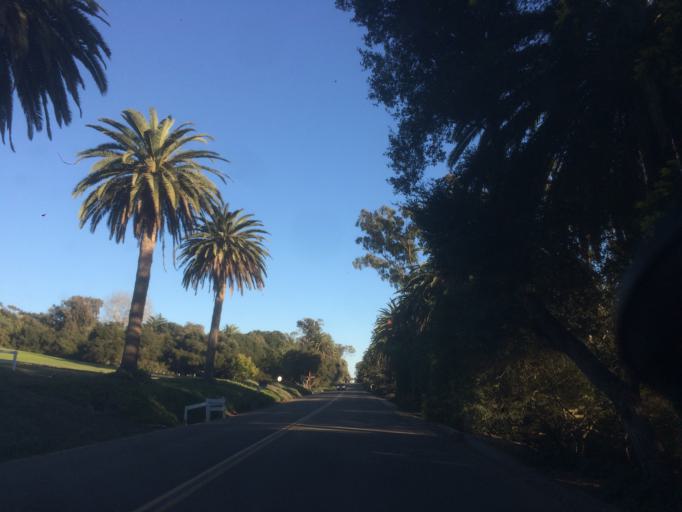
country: US
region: California
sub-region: Santa Barbara County
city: Mission Canyon
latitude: 34.4120
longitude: -119.7652
